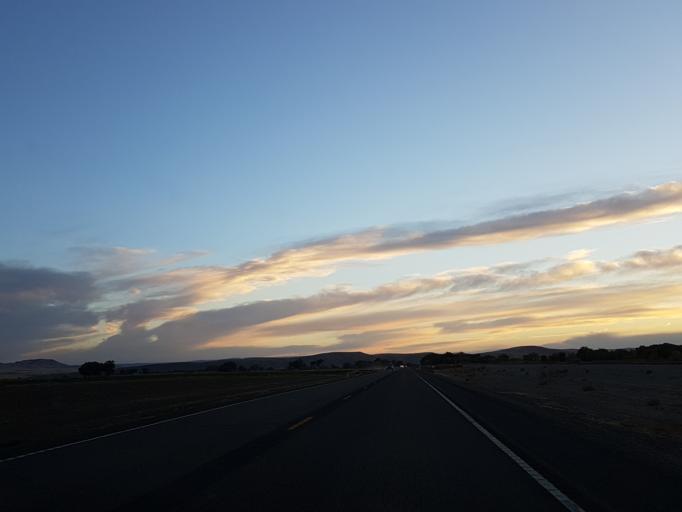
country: US
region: Oregon
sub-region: Malheur County
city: Vale
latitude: 43.9477
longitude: -117.2976
